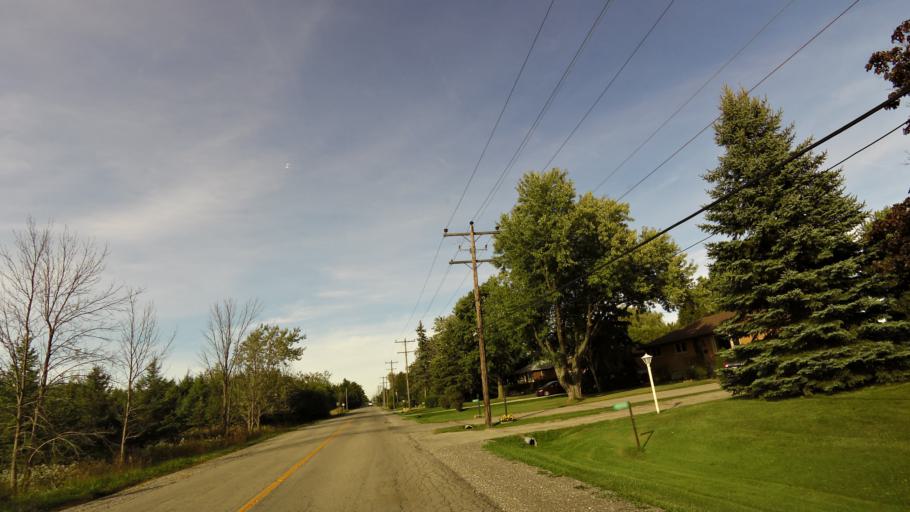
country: CA
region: Ontario
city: Ancaster
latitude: 43.1349
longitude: -79.9608
